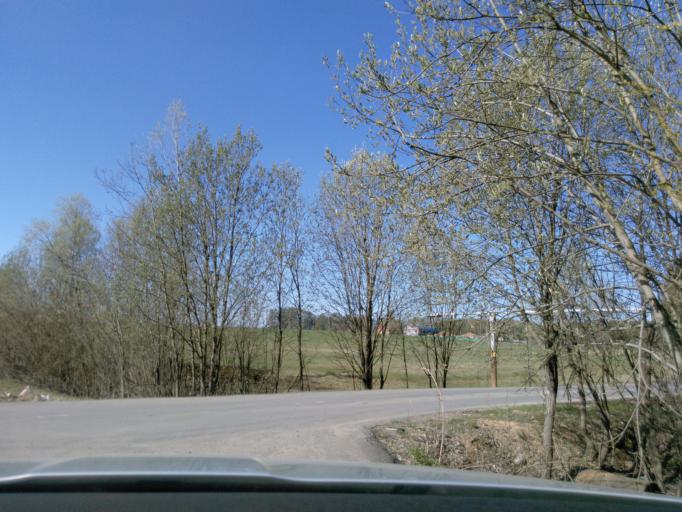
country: RU
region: Moskovskaya
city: Mendeleyevo
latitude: 56.0600
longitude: 37.2310
